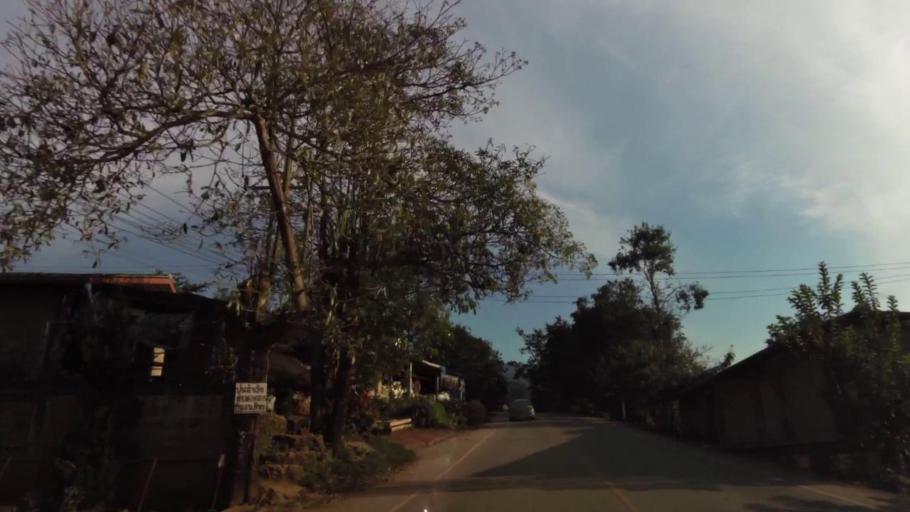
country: TH
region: Chiang Rai
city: Khun Tan
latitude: 19.8682
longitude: 100.4008
